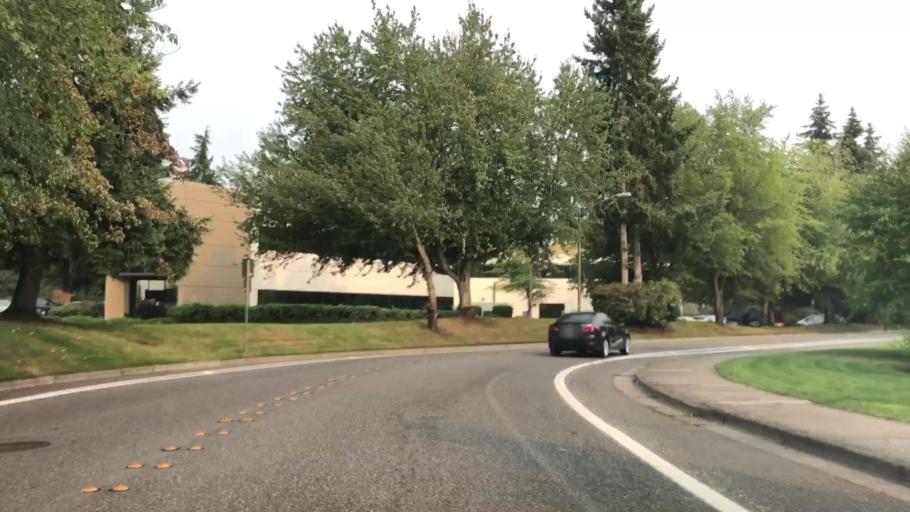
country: US
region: Washington
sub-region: King County
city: Redmond
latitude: 47.6519
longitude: -122.1408
